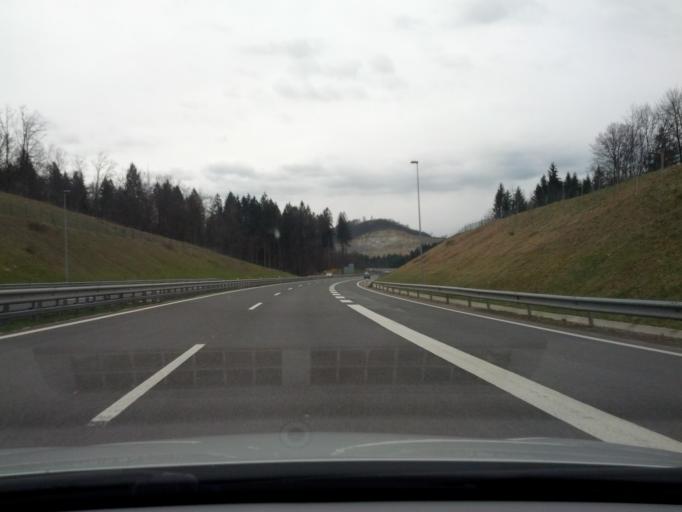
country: SI
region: Trebnje
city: Trebnje
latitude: 45.8972
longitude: 15.0560
